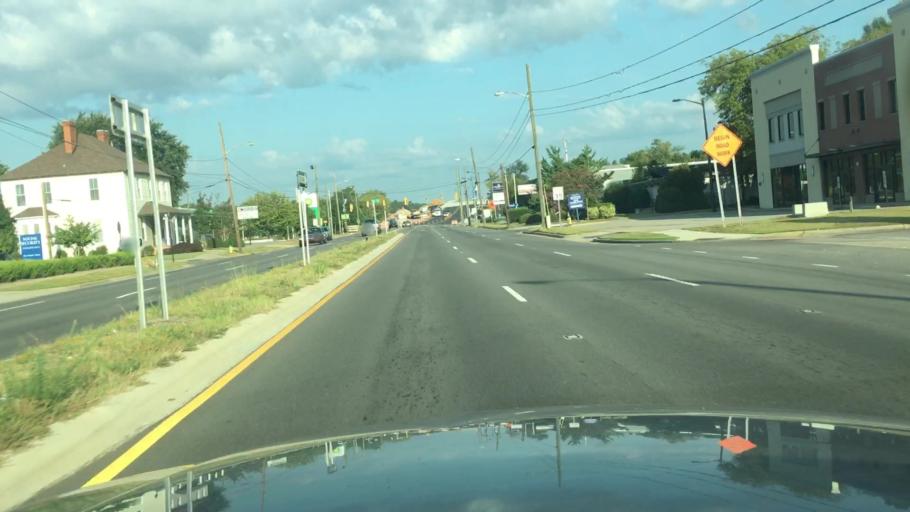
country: US
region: North Carolina
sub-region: Cumberland County
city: Fayetteville
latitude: 35.0578
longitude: -78.8783
